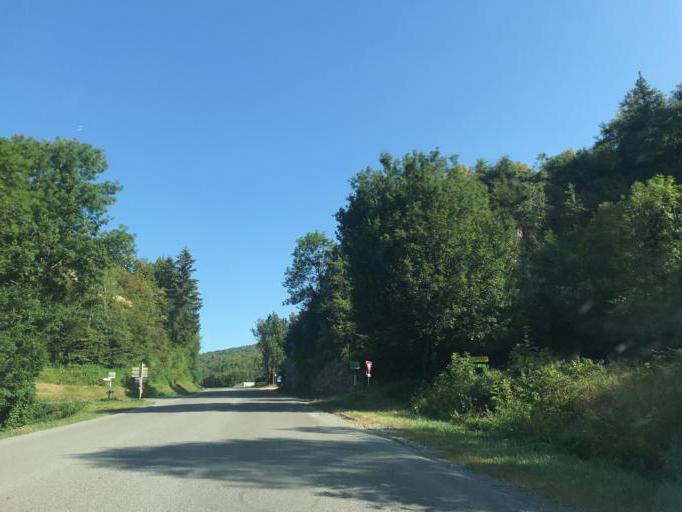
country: FR
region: Franche-Comte
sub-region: Departement du Jura
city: Lavans-les-Saint-Claude
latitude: 46.3770
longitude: 5.7555
